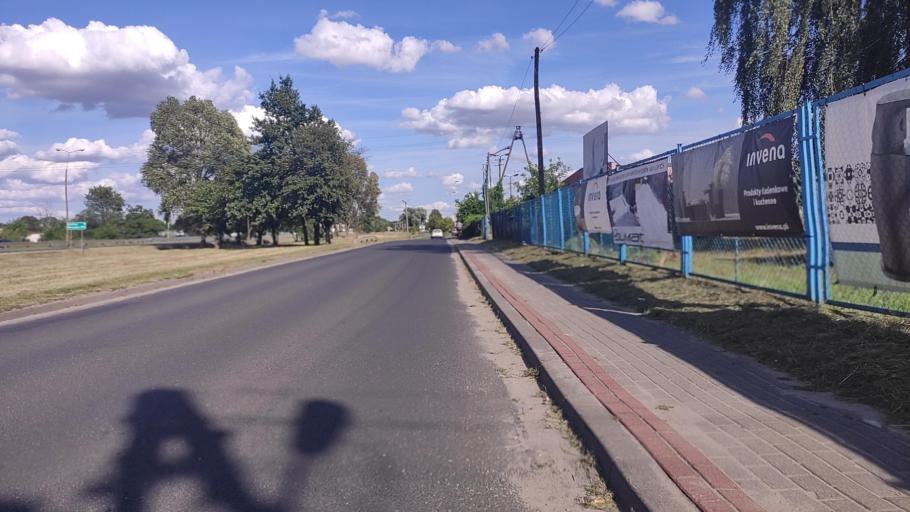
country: PL
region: Greater Poland Voivodeship
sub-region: Powiat poznanski
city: Swarzedz
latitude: 52.4059
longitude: 17.0875
